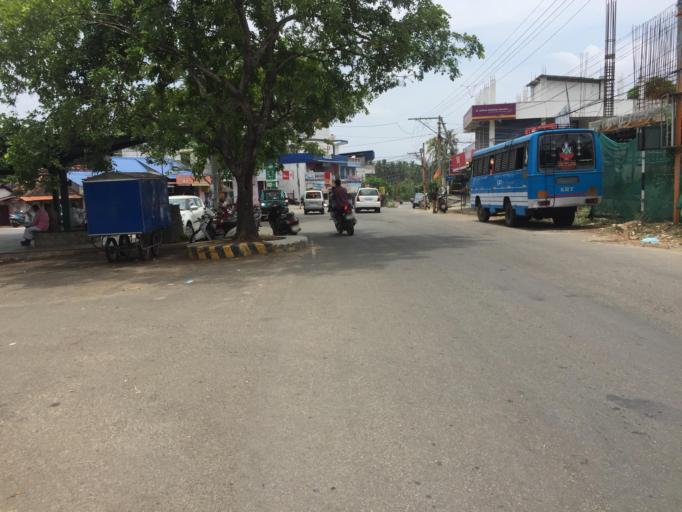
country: IN
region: Kerala
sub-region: Palakkad district
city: Chittur
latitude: 10.6835
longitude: 76.7125
